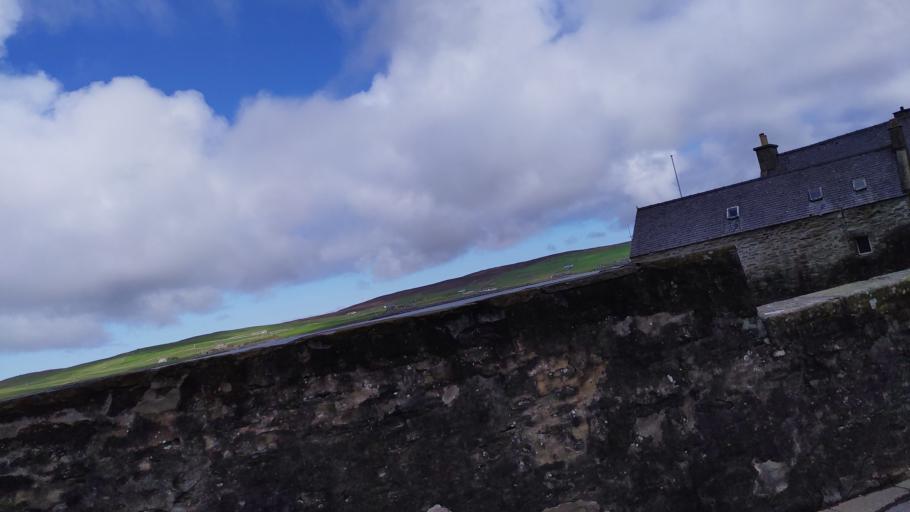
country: GB
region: Scotland
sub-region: Shetland Islands
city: Shetland
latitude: 60.1529
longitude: -1.1398
